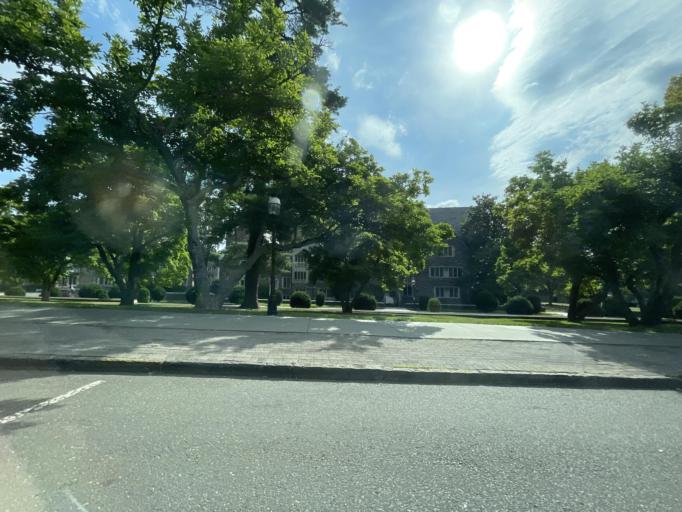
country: US
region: New Jersey
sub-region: Mercer County
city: Princeton
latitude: 40.3451
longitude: -74.6604
